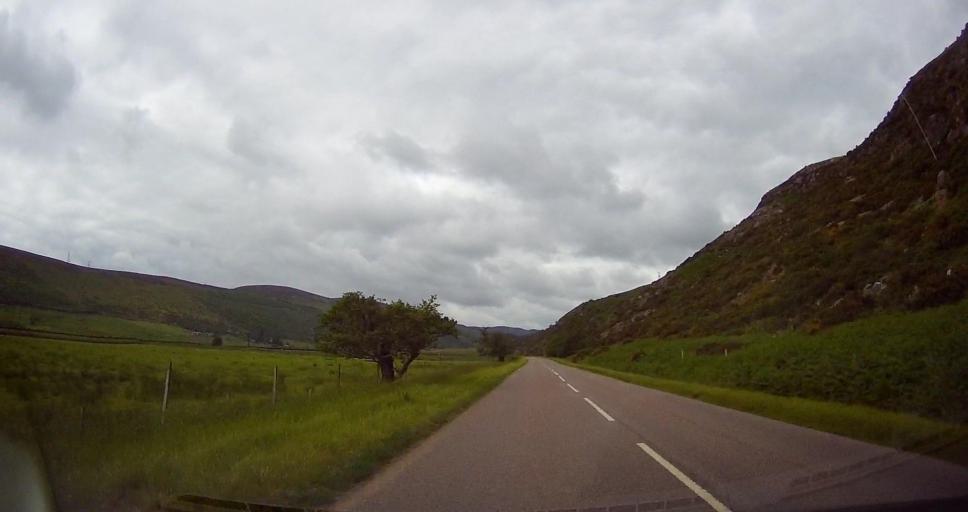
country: GB
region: Scotland
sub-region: Highland
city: Dornoch
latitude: 57.9819
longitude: -4.1191
